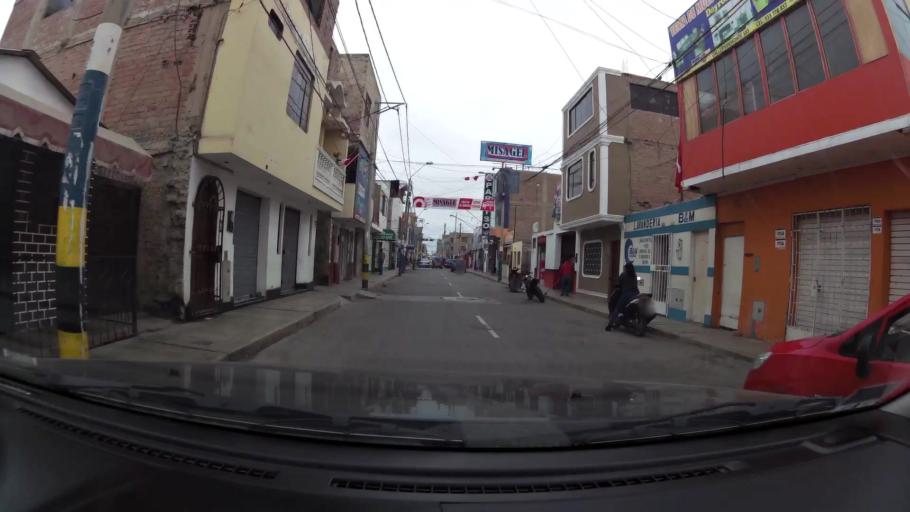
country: PE
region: Ica
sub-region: Provincia de Pisco
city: Pisco
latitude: -13.7135
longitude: -76.2049
